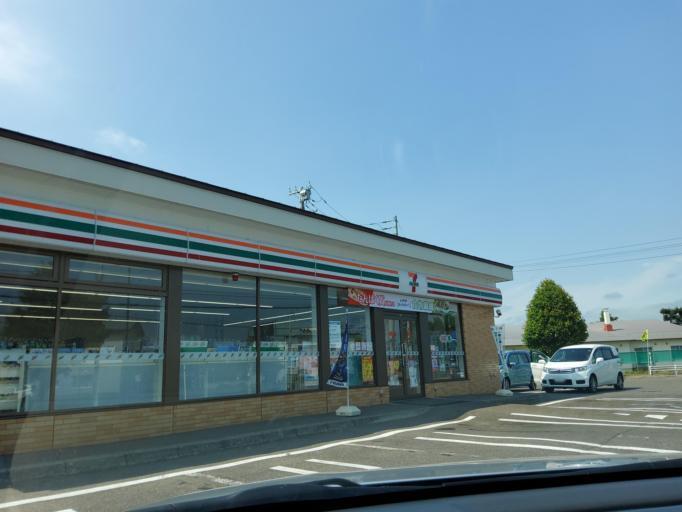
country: JP
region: Hokkaido
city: Obihiro
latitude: 42.9030
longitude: 143.0494
